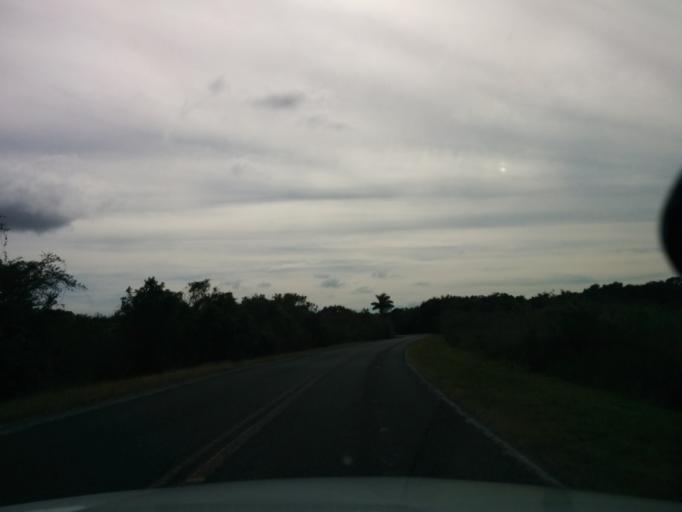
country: US
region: Florida
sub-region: Miami-Dade County
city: Florida City
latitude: 25.3863
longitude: -80.6113
